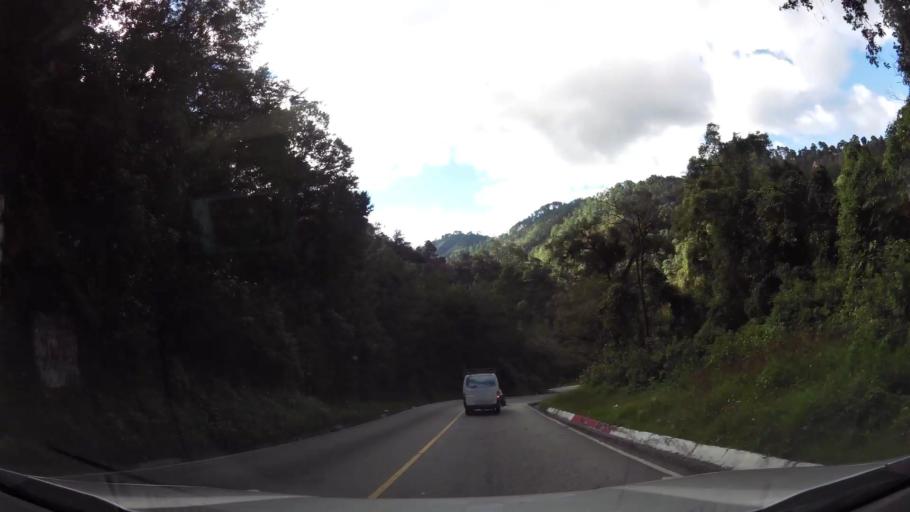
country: GT
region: Quiche
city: Chichicastenango
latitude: 14.9181
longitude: -91.1037
